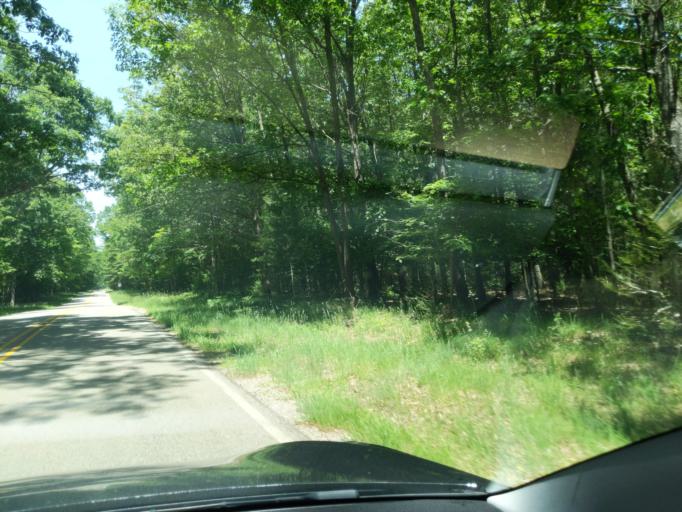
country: US
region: Michigan
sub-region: Muskegon County
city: Montague
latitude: 43.3923
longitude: -86.4162
